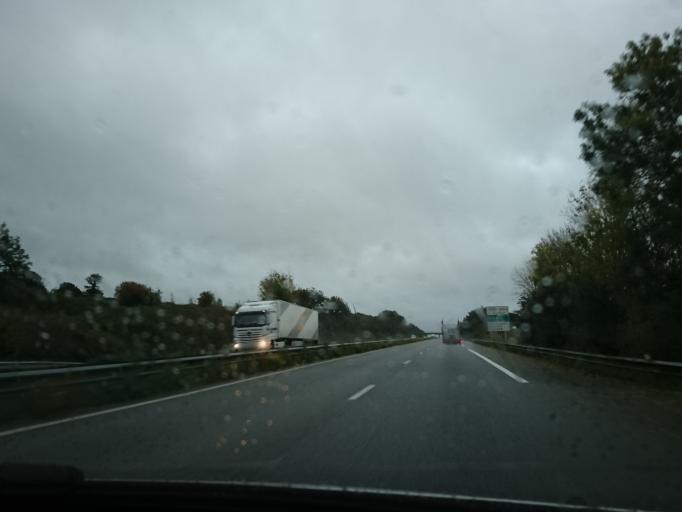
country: FR
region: Brittany
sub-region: Departement du Finistere
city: Chateaulin
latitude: 48.2215
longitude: -4.0660
